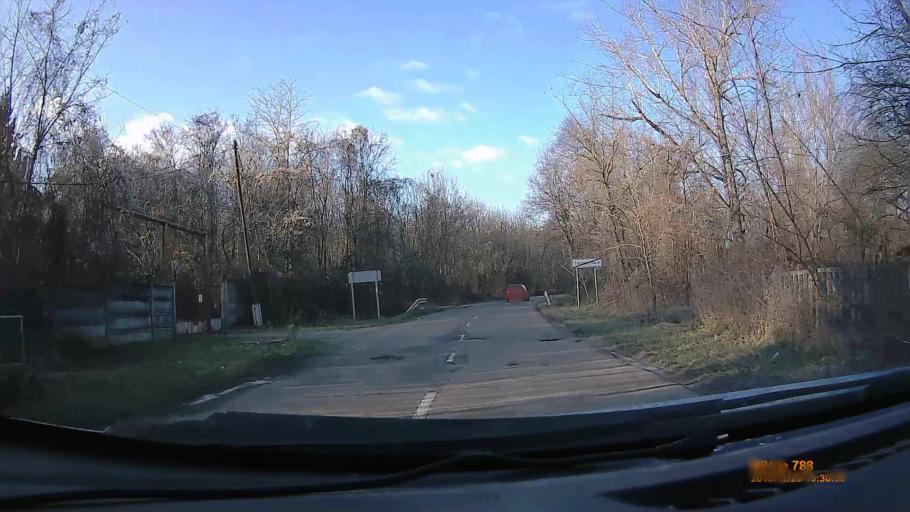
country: HU
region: Heves
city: Verpelet
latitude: 47.8792
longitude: 20.1966
